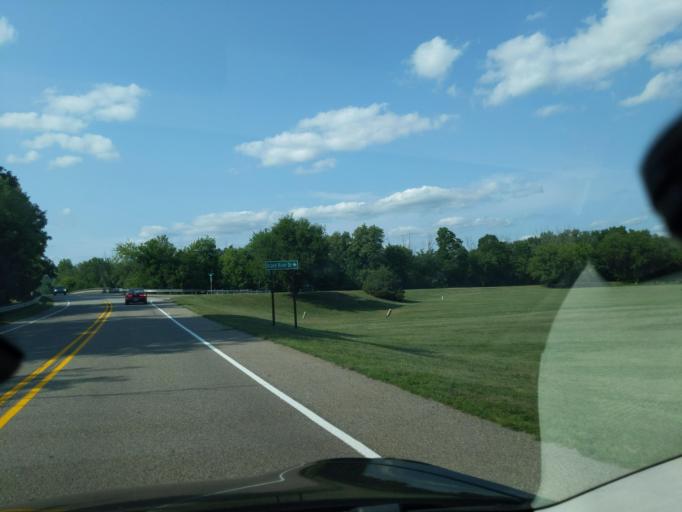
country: US
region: Michigan
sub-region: Kent County
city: Lowell
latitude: 42.9281
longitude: -85.3315
